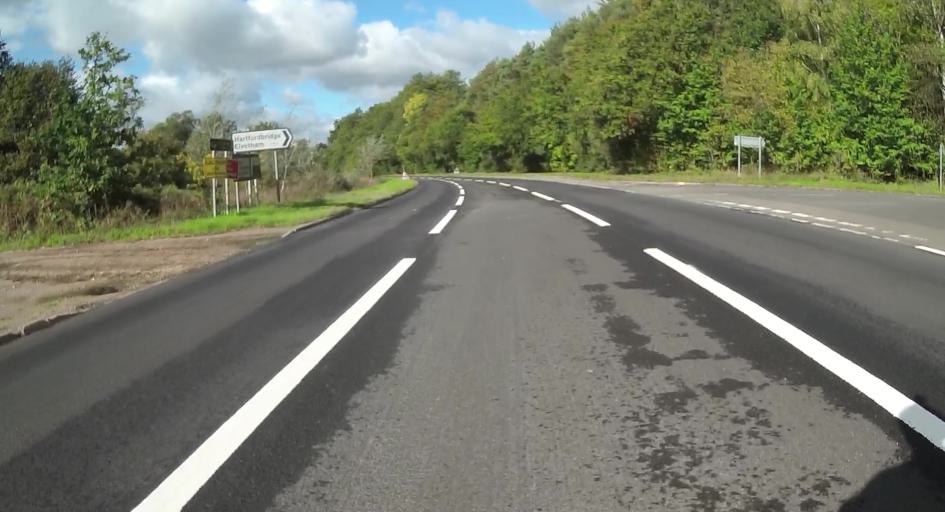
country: GB
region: England
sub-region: Hampshire
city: Fleet
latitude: 51.2955
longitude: -0.8715
